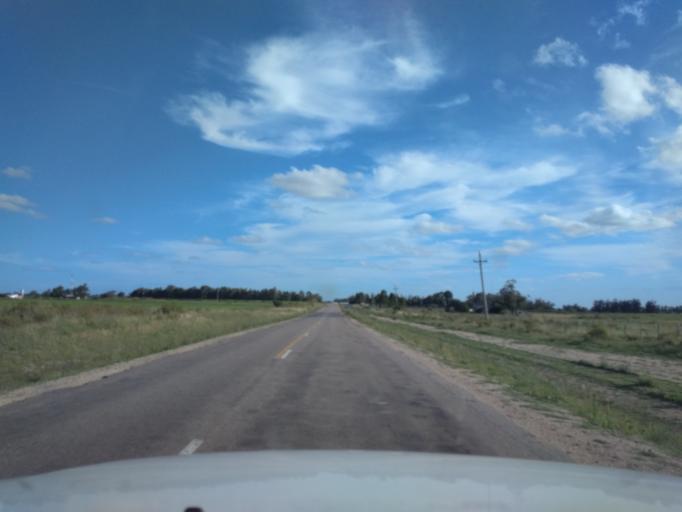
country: UY
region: Canelones
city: San Ramon
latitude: -34.2345
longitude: -55.9275
